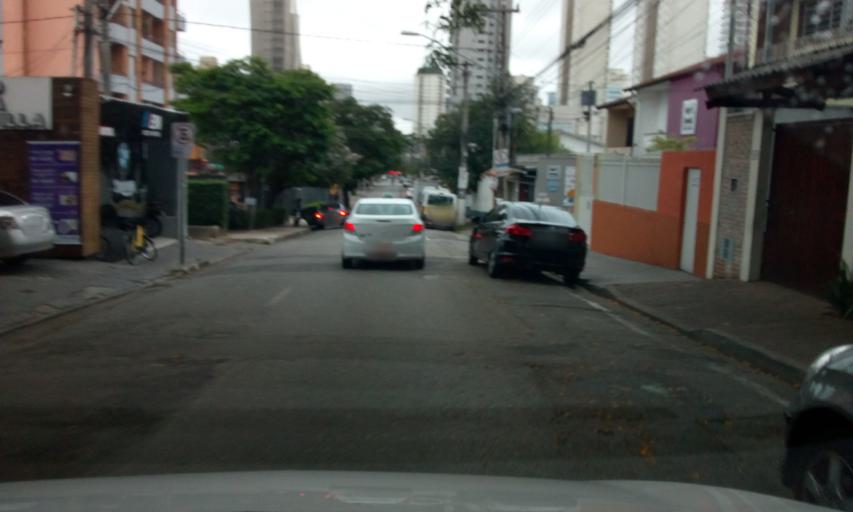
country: BR
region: Sao Paulo
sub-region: Sao Paulo
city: Sao Paulo
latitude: -23.6027
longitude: -46.6780
